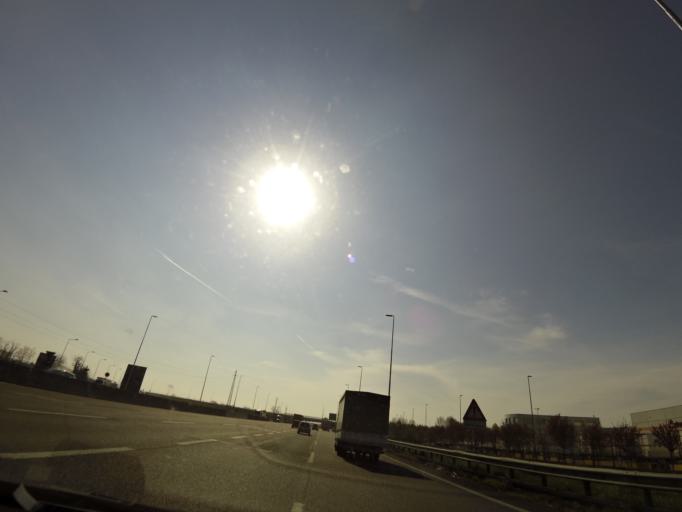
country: IT
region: Lombardy
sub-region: Citta metropolitana di Milano
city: Chiaravalle
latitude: 45.4438
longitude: 9.2404
